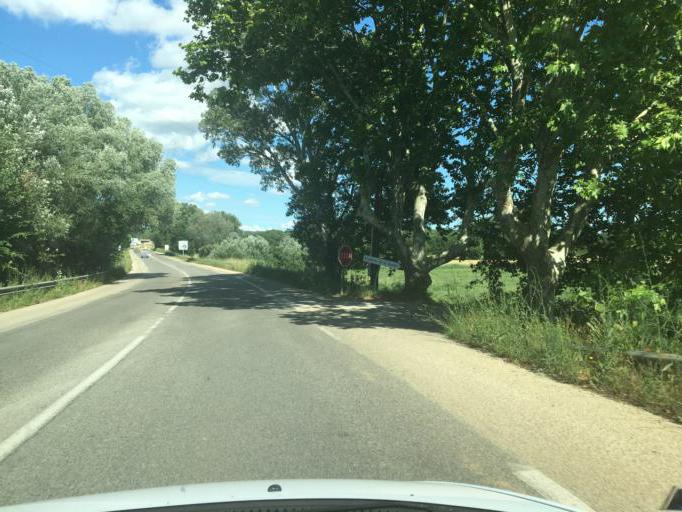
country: FR
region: Provence-Alpes-Cote d'Azur
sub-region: Departement des Bouches-du-Rhone
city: Eguilles
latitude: 43.5437
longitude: 5.3537
